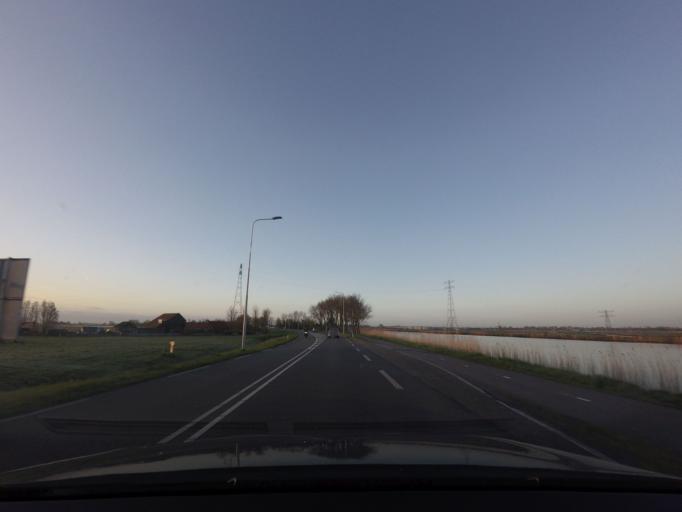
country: NL
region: North Holland
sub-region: Gemeente Uitgeest
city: Uitgeest
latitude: 52.5286
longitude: 4.7793
